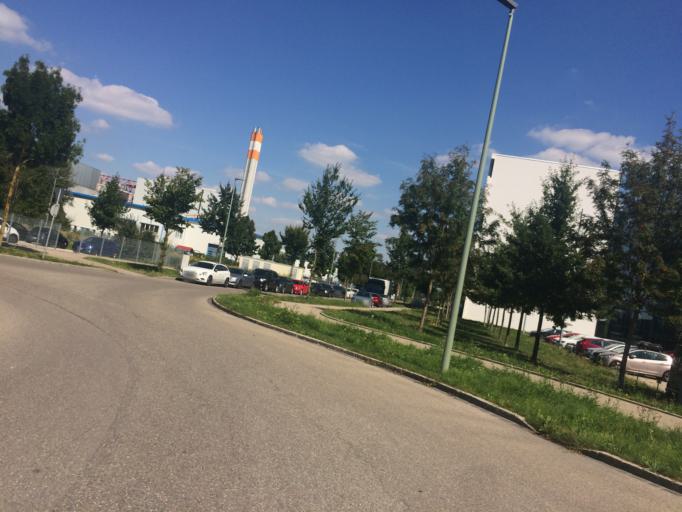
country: DE
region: Bavaria
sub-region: Swabia
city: Augsburg
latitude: 48.4001
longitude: 10.9297
